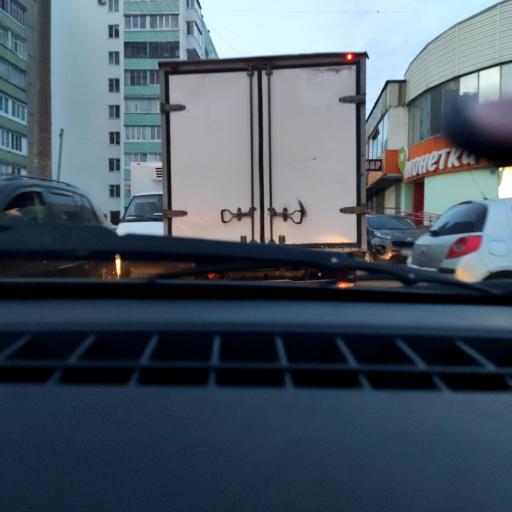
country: RU
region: Bashkortostan
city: Ufa
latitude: 54.7714
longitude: 56.0537
